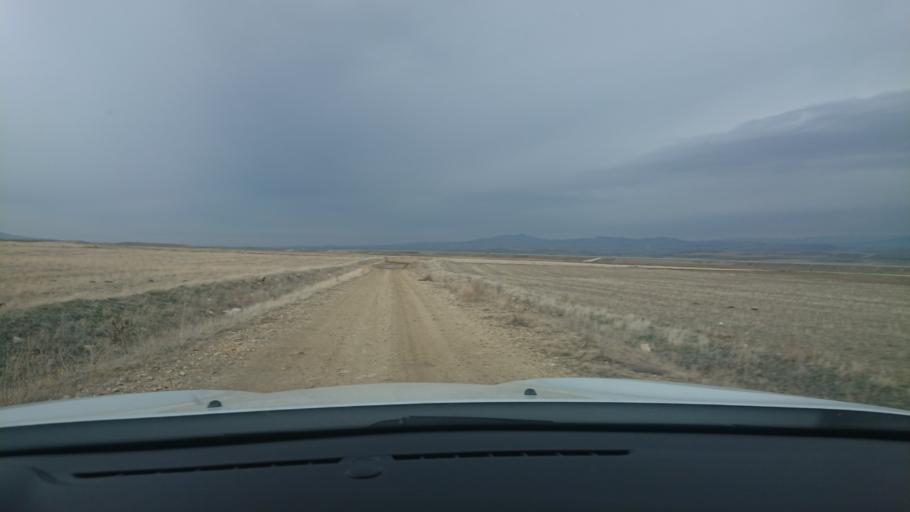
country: TR
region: Aksaray
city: Sariyahsi
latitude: 38.9810
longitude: 33.8785
